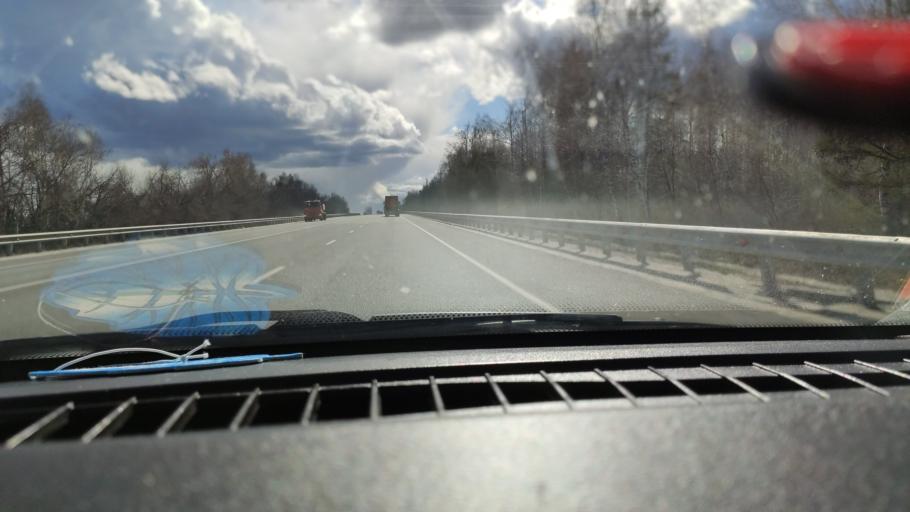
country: RU
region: Saratov
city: Khvalynsk
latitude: 52.5608
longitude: 48.0885
